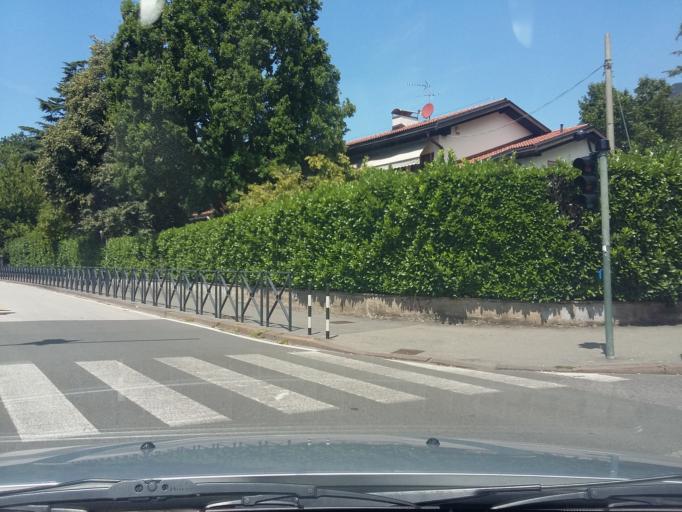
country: IT
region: Trentino-Alto Adige
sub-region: Bolzano
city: Bolzano
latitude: 46.4903
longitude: 11.3254
